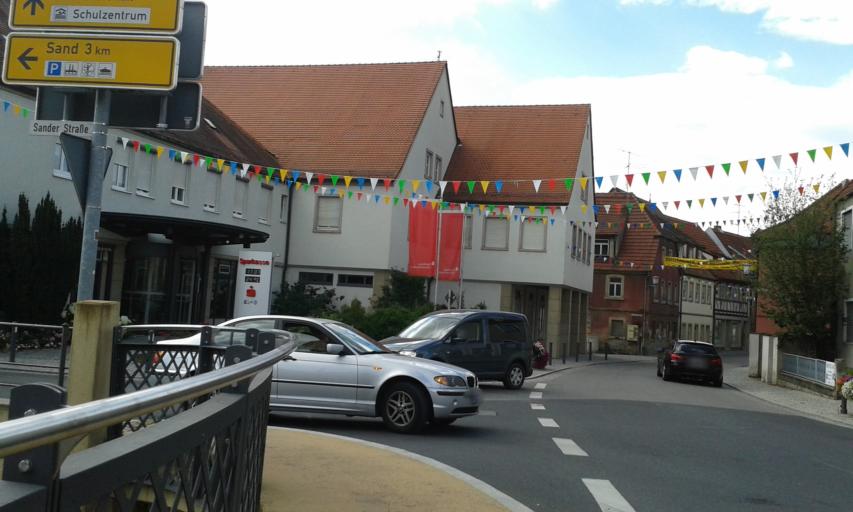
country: DE
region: Bavaria
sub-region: Regierungsbezirk Unterfranken
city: Zeil
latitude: 50.0080
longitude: 10.5955
